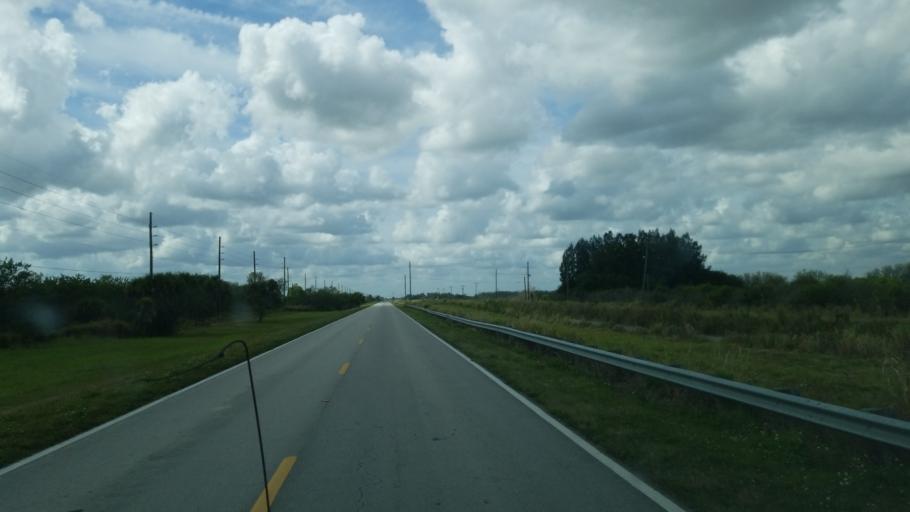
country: US
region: Florida
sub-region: Saint Lucie County
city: Lakewood Park
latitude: 27.4475
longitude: -80.5074
